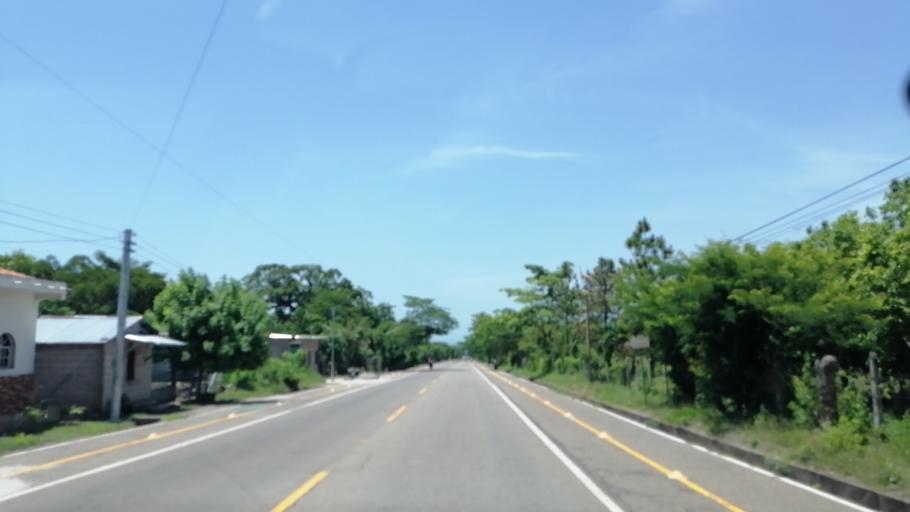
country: SV
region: Chalatenango
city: Nueva Concepcion
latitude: 14.1414
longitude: -89.2974
